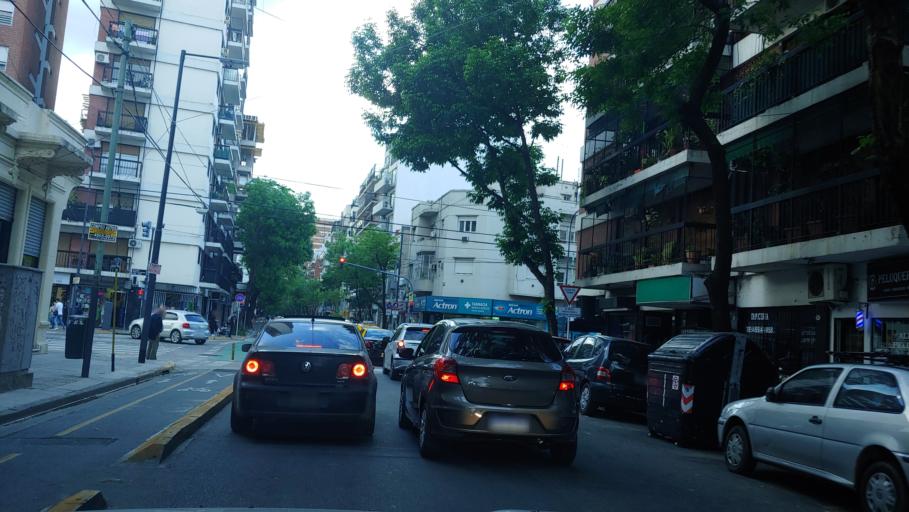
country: AR
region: Buenos Aires F.D.
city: Colegiales
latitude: -34.5727
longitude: -58.4460
